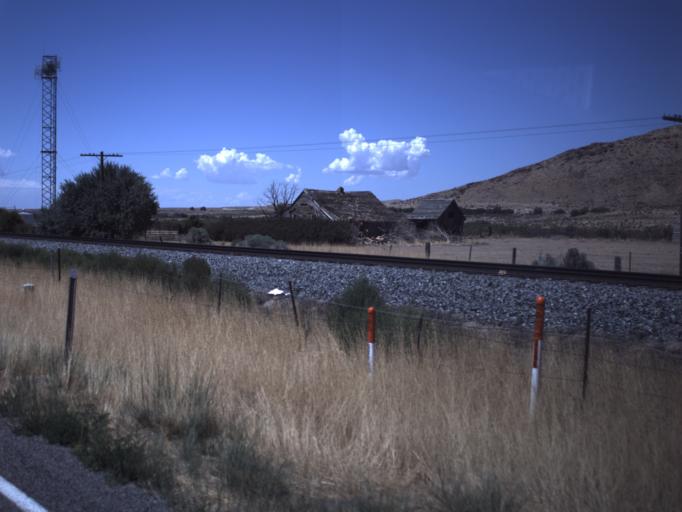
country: US
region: Utah
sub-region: Millard County
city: Delta
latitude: 39.5374
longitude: -112.2629
